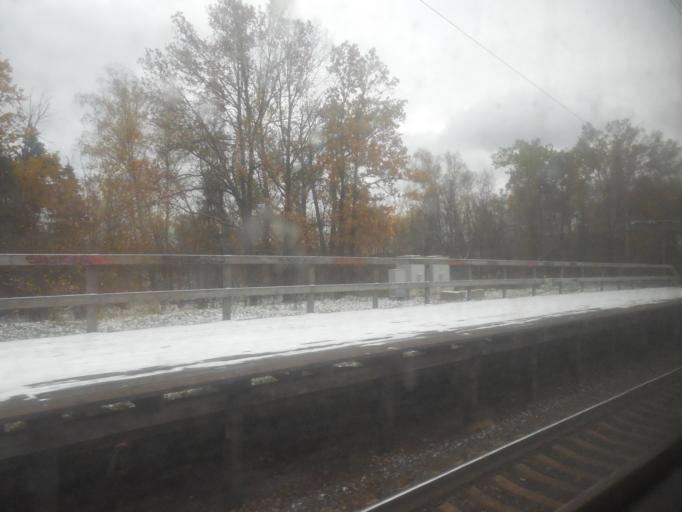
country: RU
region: Moskovskaya
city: Novoivanovskoye
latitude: 55.6967
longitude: 37.3379
